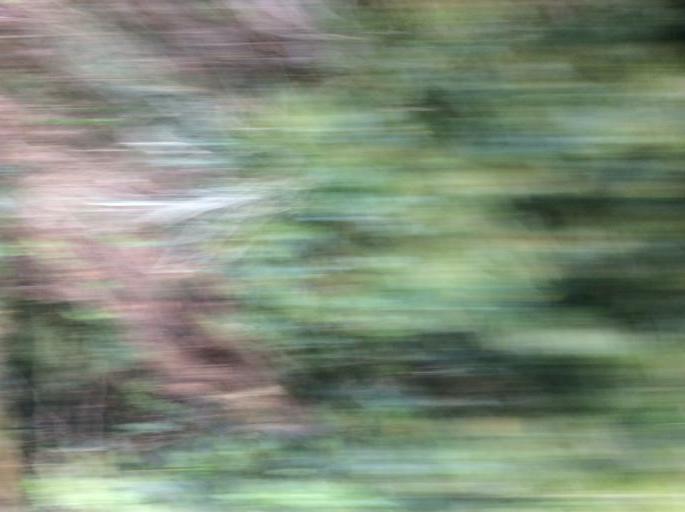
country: TW
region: Taipei
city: Taipei
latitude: 25.1719
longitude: 121.5406
